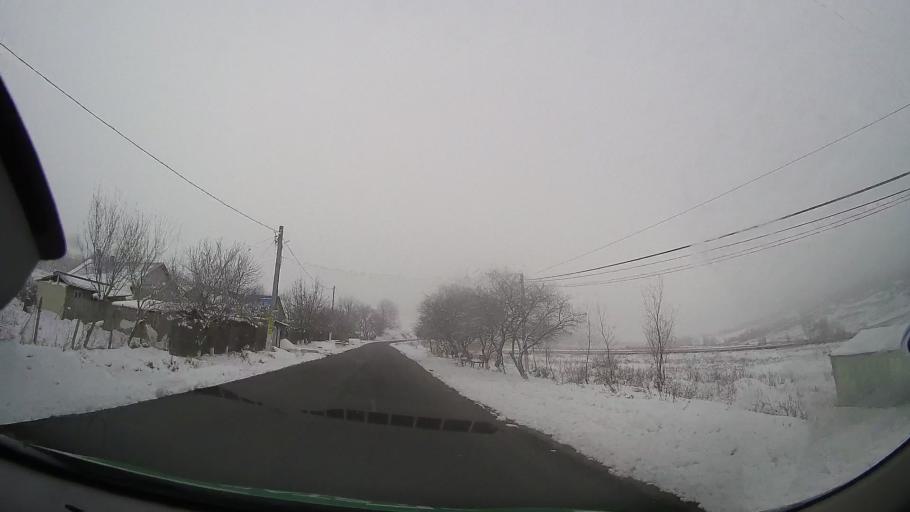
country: RO
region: Bacau
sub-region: Comuna Oncesti
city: Oncesti
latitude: 46.4843
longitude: 27.2557
